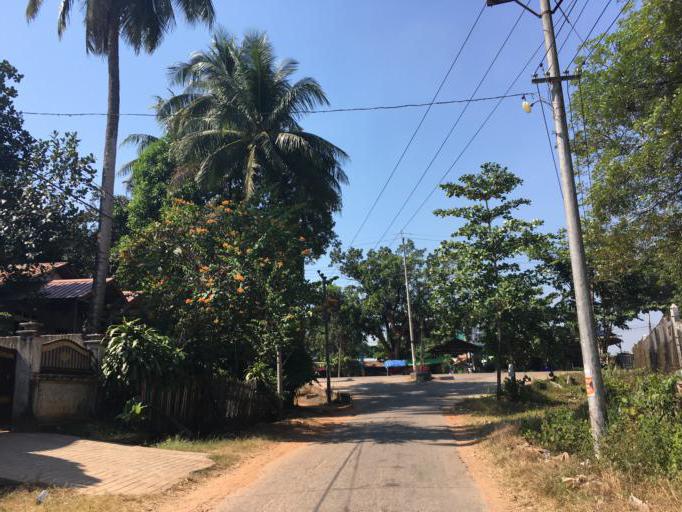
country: MM
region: Mon
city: Mawlamyine
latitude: 16.4340
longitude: 97.6974
